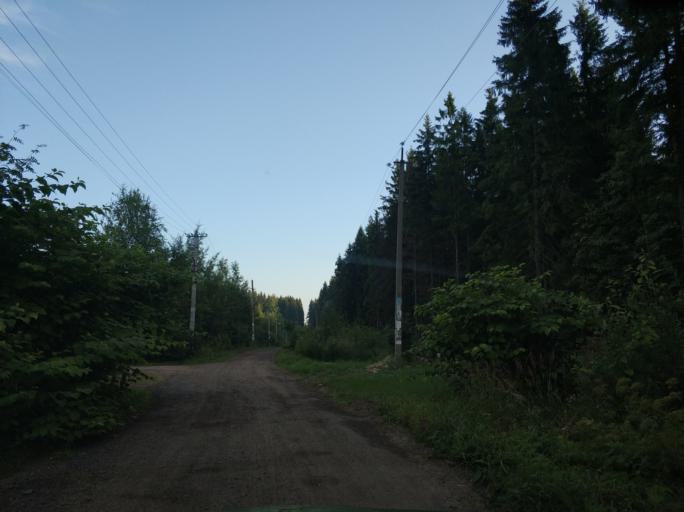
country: RU
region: Leningrad
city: Shcheglovo
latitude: 60.0535
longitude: 30.7515
